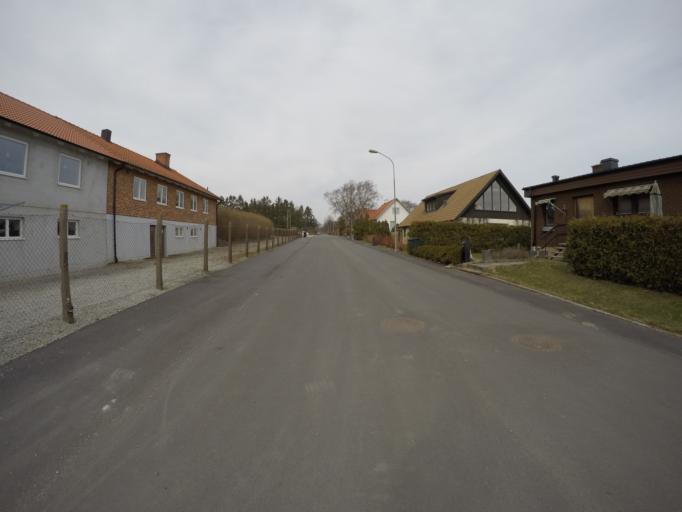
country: SE
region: Skane
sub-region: Ystads Kommun
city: Kopingebro
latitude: 55.4367
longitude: 14.1098
